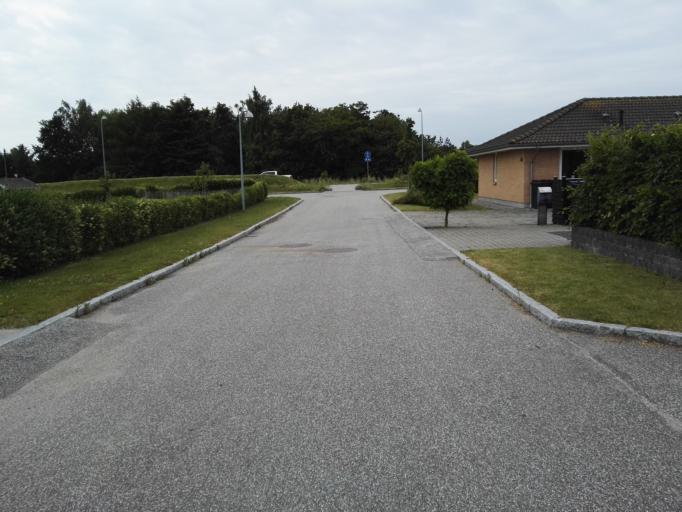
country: DK
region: Capital Region
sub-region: Egedal Kommune
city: Olstykke
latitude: 55.7870
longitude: 12.1512
